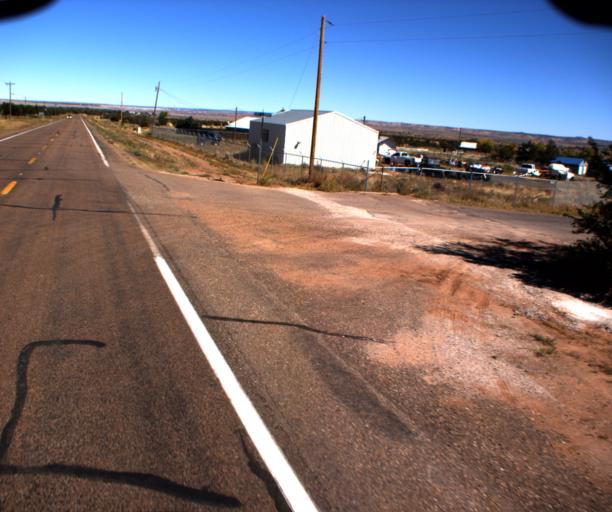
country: US
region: Arizona
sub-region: Apache County
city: Saint Johns
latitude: 34.4702
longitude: -109.3929
